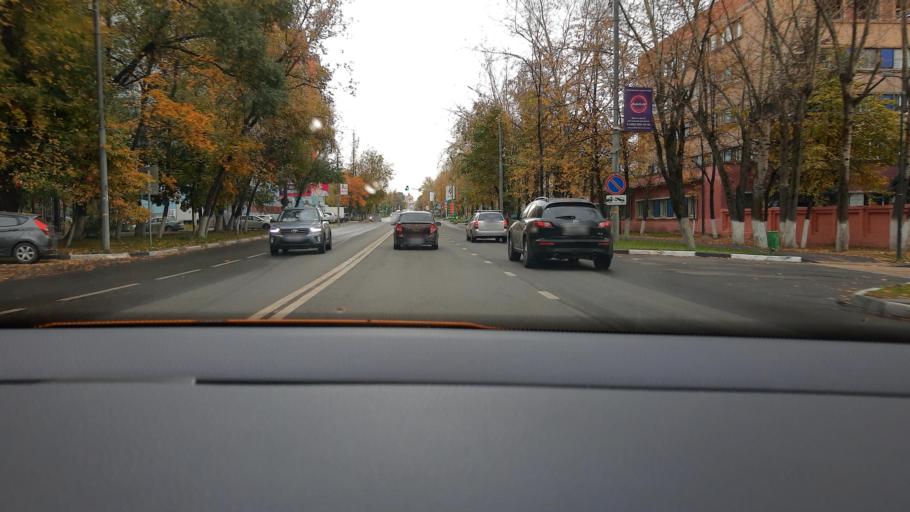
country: RU
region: Moskovskaya
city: Reutov
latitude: 55.7677
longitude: 37.8471
